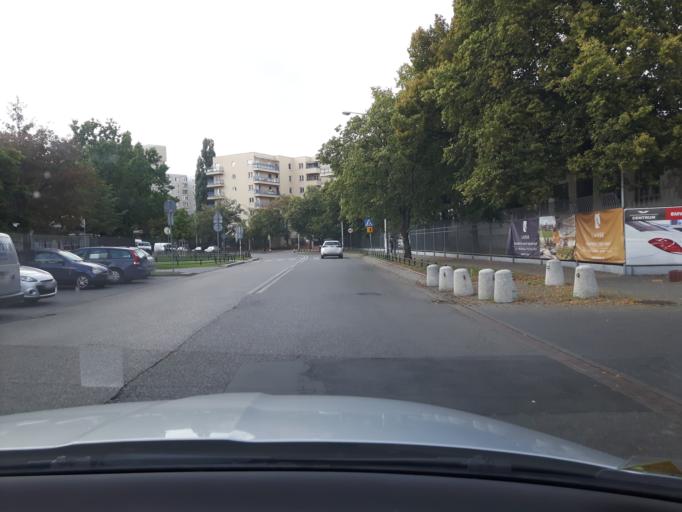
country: PL
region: Masovian Voivodeship
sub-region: Warszawa
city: Mokotow
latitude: 52.1897
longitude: 21.0560
